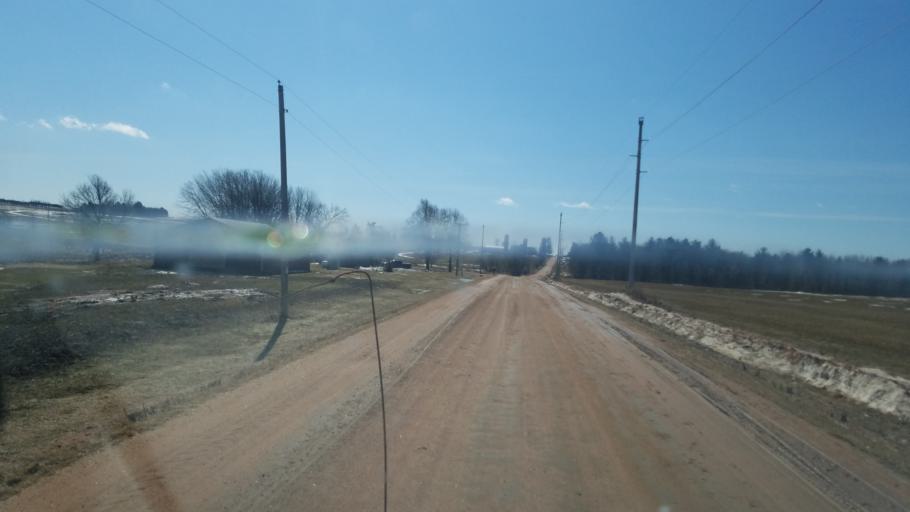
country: US
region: Wisconsin
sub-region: Clark County
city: Loyal
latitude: 44.5914
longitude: -90.3959
